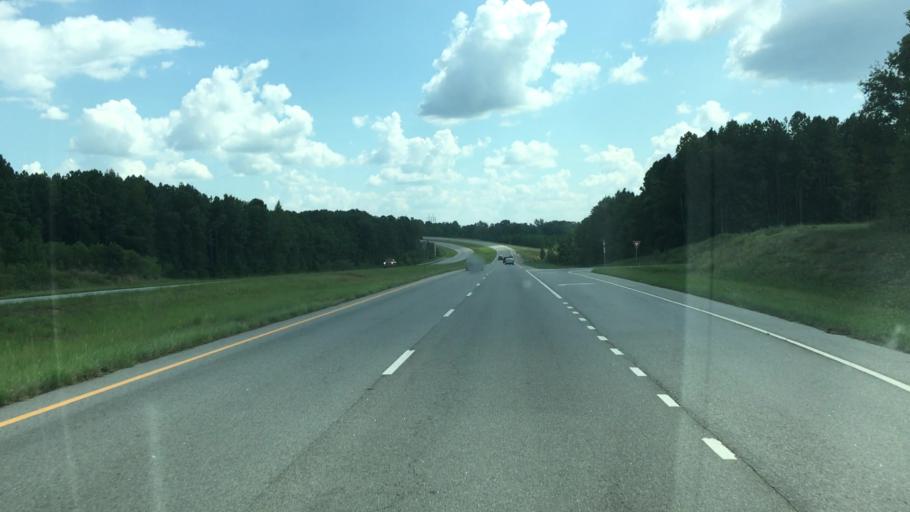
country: US
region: Georgia
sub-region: Putnam County
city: Eatonton
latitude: 33.2831
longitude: -83.3710
